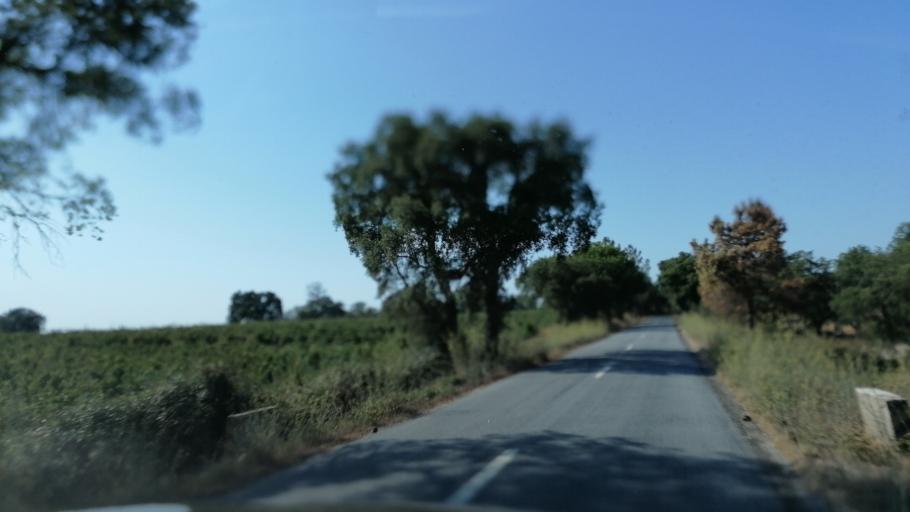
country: PT
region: Santarem
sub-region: Benavente
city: Poceirao
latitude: 38.7467
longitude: -8.6307
